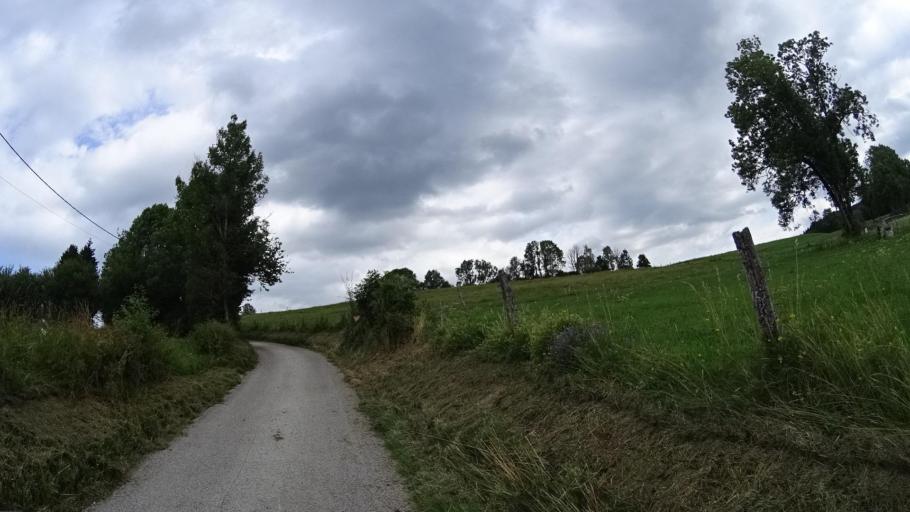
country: FR
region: Franche-Comte
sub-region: Departement du Doubs
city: Les Fourgs
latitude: 46.8370
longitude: 6.3468
